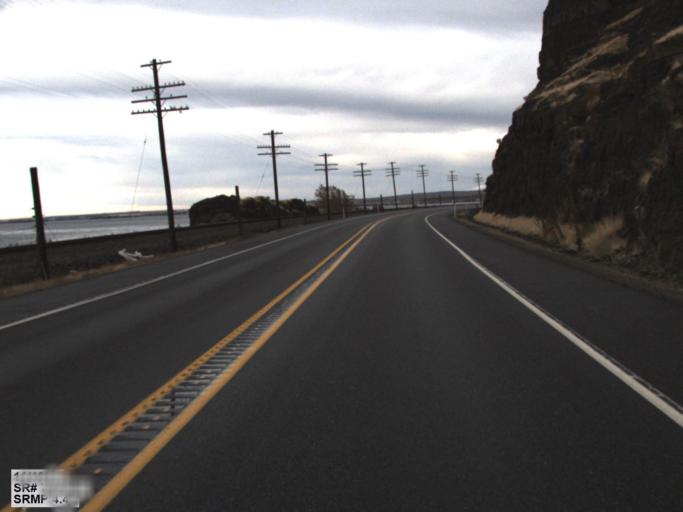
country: US
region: Washington
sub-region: Benton County
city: Finley
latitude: 46.0495
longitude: -118.9379
